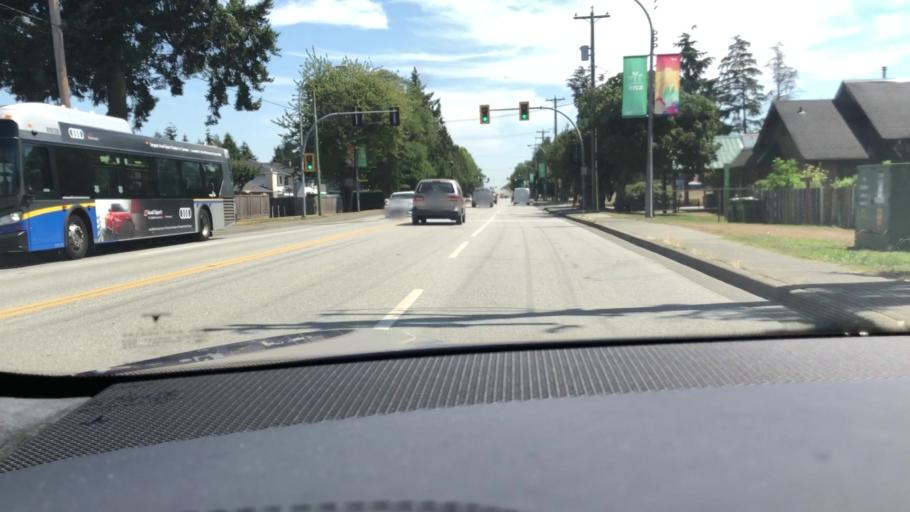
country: CA
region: British Columbia
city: Richmond
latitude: 49.1845
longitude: -123.0870
